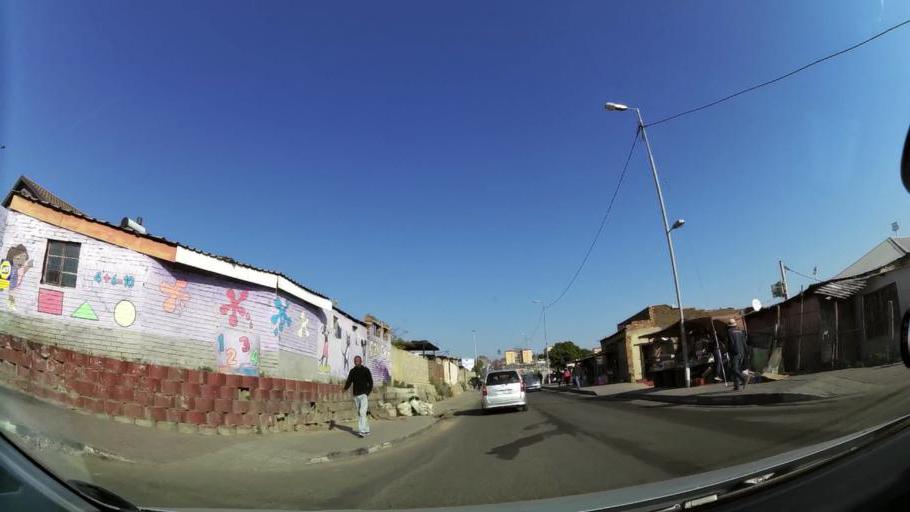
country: ZA
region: Gauteng
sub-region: City of Johannesburg Metropolitan Municipality
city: Modderfontein
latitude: -26.1073
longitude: 28.1025
